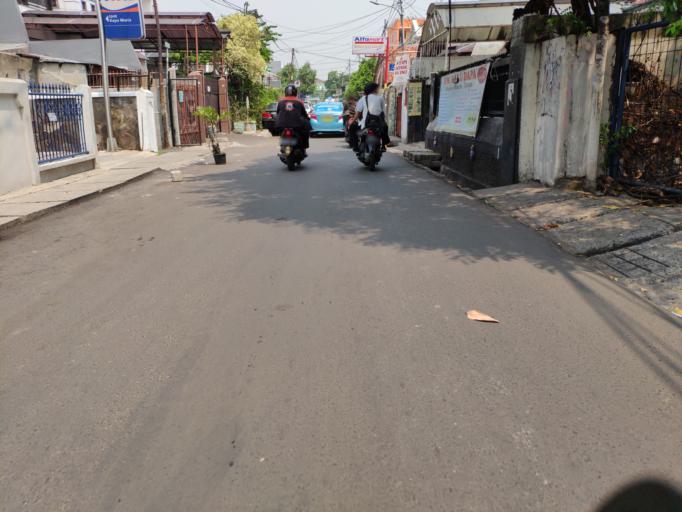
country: ID
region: Jakarta Raya
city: Jakarta
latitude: -6.2065
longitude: 106.8623
